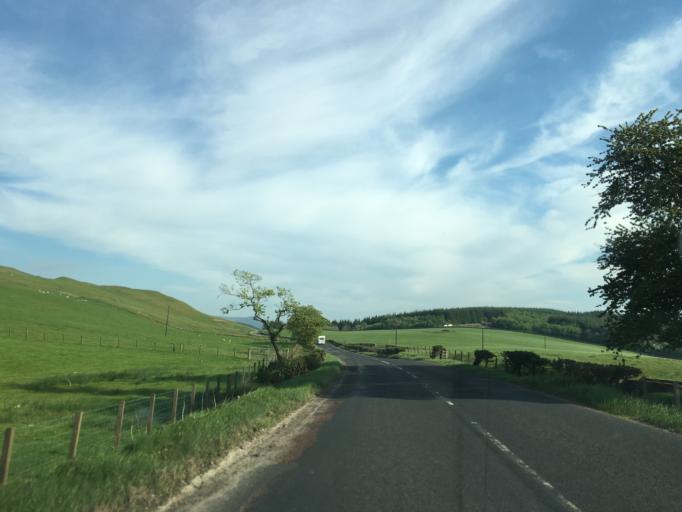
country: GB
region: Scotland
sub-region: South Lanarkshire
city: Biggar
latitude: 55.6505
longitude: -3.4331
